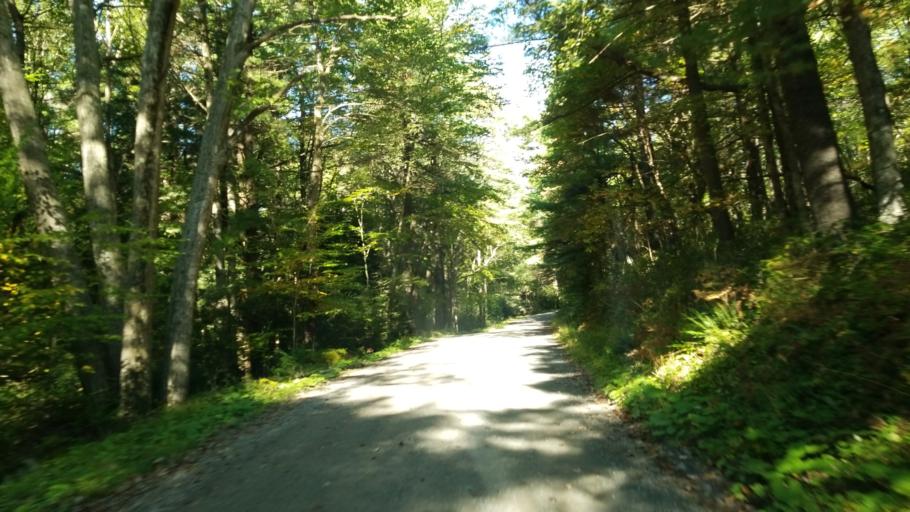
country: US
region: Pennsylvania
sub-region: Clearfield County
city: Hyde
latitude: 41.0866
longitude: -78.5326
